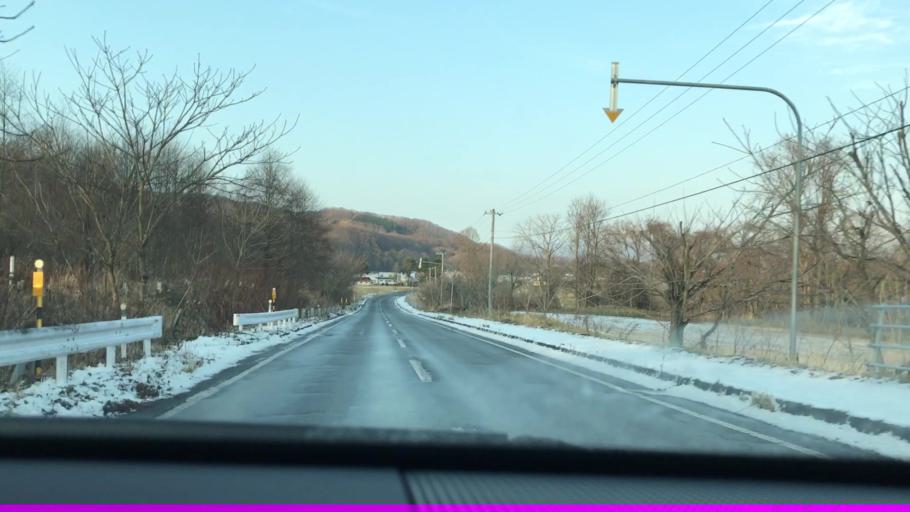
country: JP
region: Hokkaido
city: Shizunai-furukawacho
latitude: 42.4139
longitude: 142.3971
